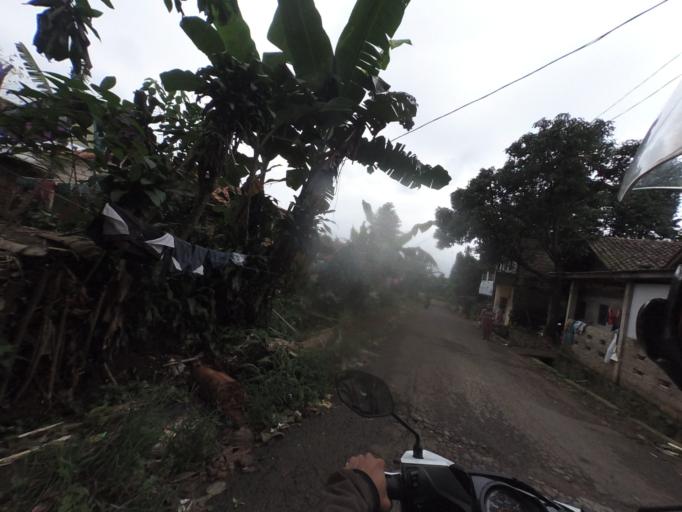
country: ID
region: West Java
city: Bogor
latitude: -6.6304
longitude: 106.7447
